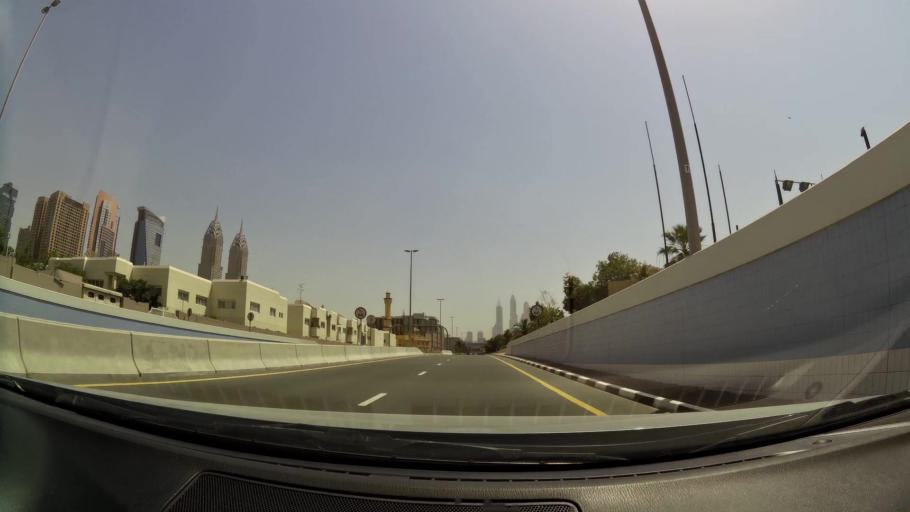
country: AE
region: Dubai
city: Dubai
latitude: 25.1081
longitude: 55.1705
